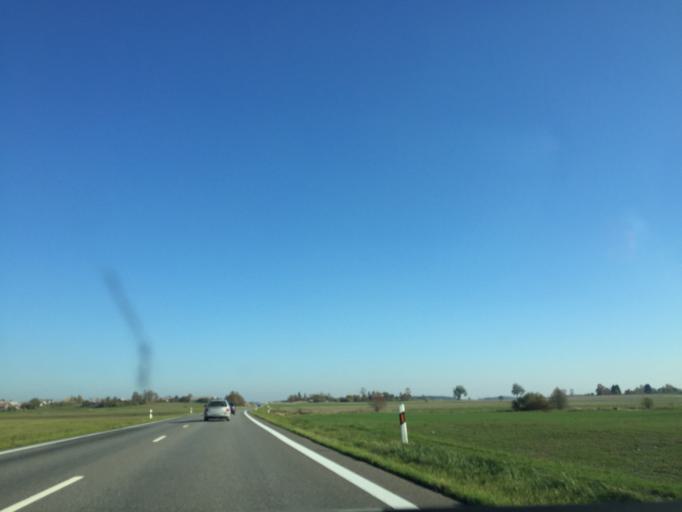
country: LT
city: Salantai
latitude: 55.9234
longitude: 21.5296
